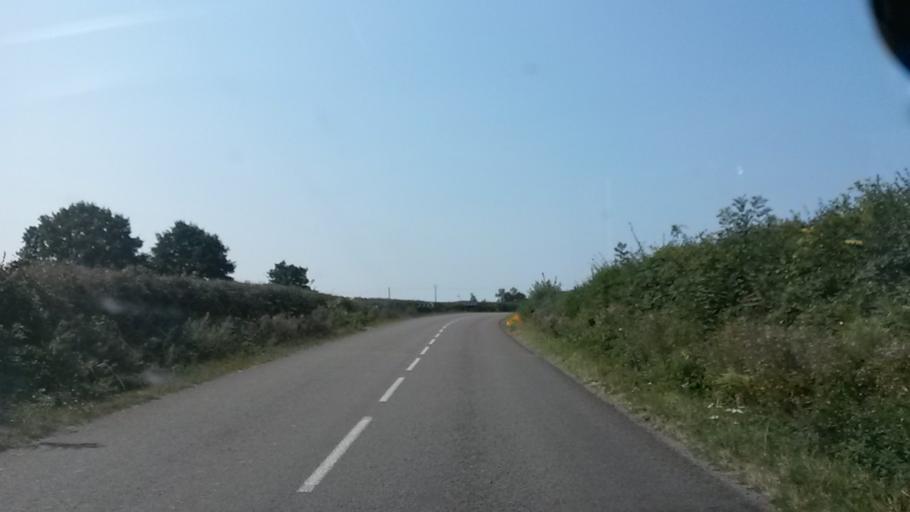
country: FR
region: Pays de la Loire
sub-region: Departement de la Mayenne
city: Saint-Pierre-des-Nids
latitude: 48.3905
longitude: -0.1188
